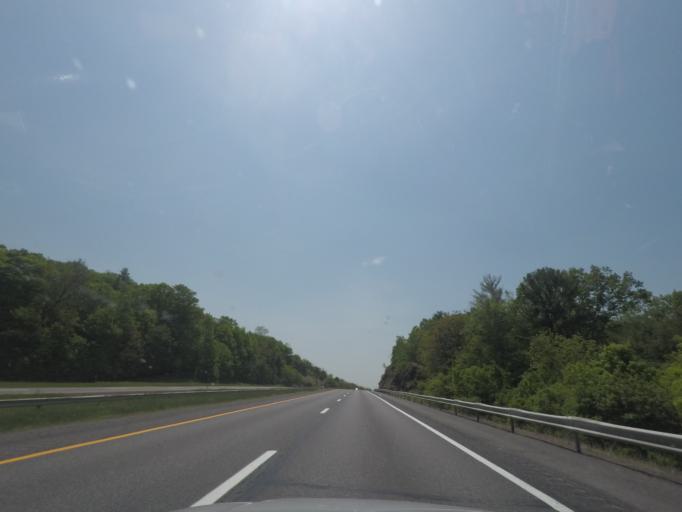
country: US
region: New York
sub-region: Greene County
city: Coxsackie
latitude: 42.3603
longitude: -73.8487
